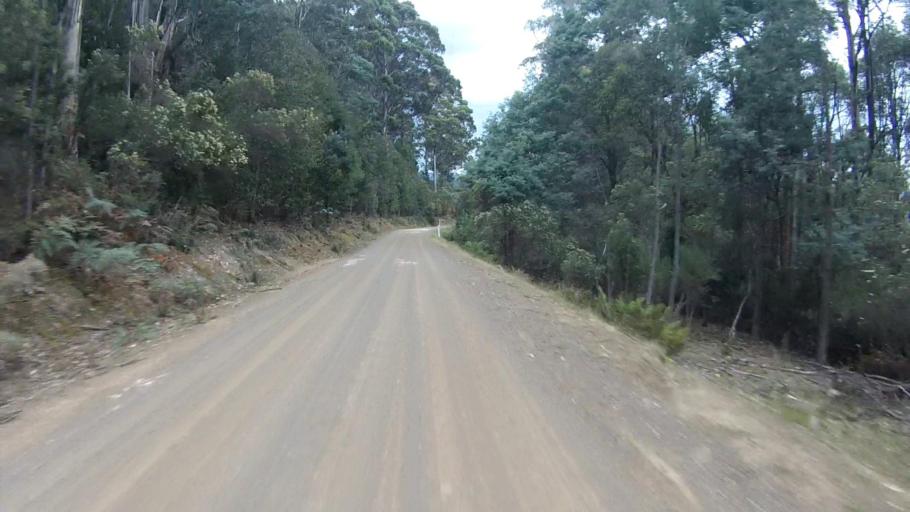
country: AU
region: Tasmania
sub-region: Huon Valley
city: Huonville
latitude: -42.9551
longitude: 147.0472
